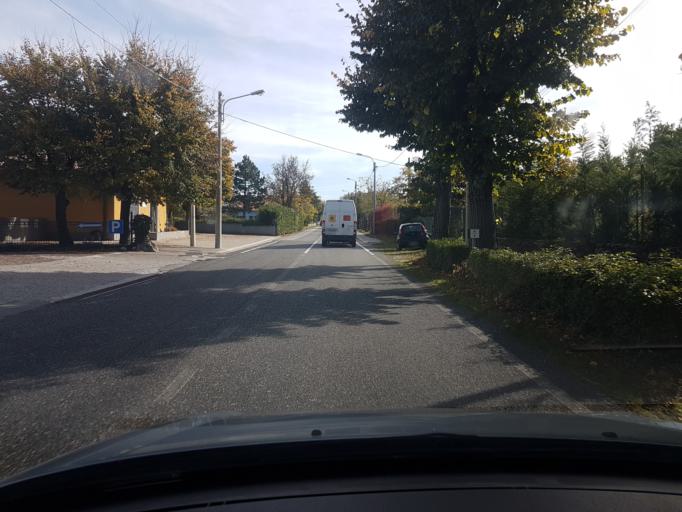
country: IT
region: Friuli Venezia Giulia
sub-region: Provincia di Trieste
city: Prosecco-Contovello
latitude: 45.7168
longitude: 13.7253
